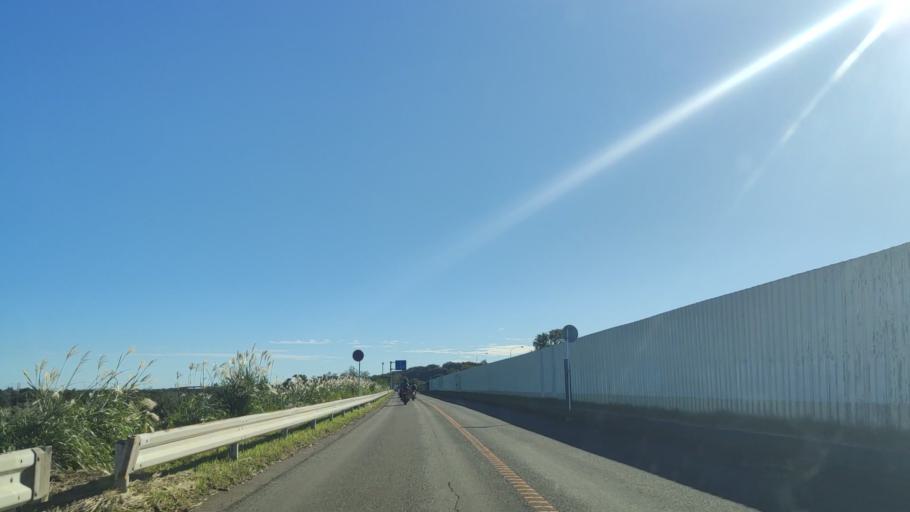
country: JP
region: Kanagawa
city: Zama
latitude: 35.5047
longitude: 139.3729
